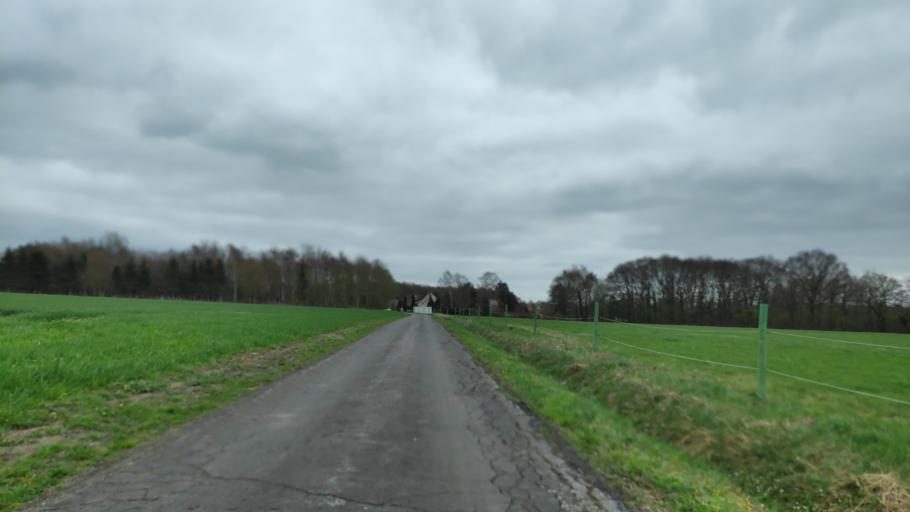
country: DE
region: North Rhine-Westphalia
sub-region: Regierungsbezirk Detmold
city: Petershagen
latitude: 52.3640
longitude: 8.8968
